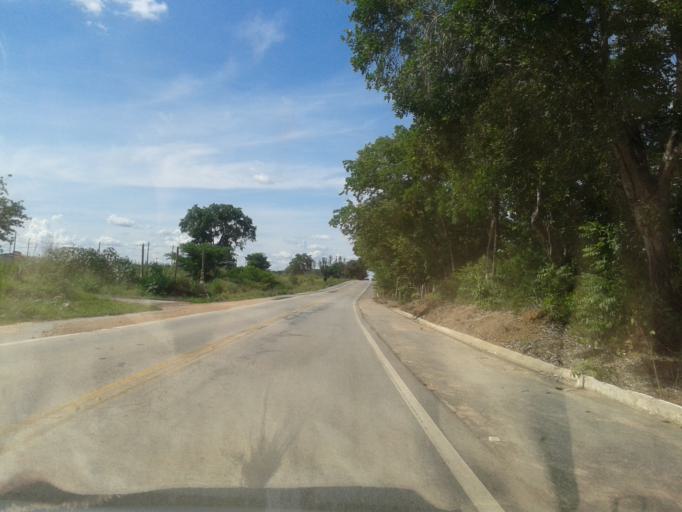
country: BR
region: Goias
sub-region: Itapuranga
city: Itapuranga
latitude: -15.4375
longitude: -50.3695
